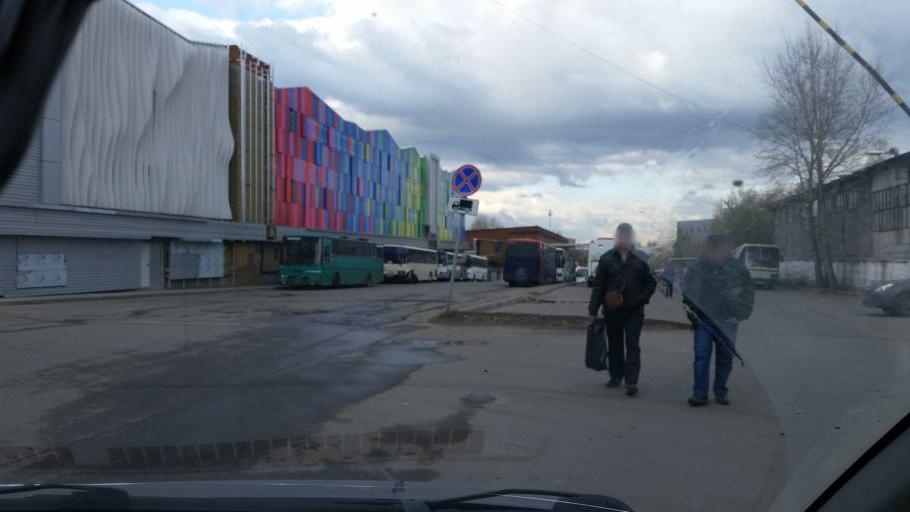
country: RU
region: Moscow
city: Kotlovka
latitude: 55.6752
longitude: 37.6137
